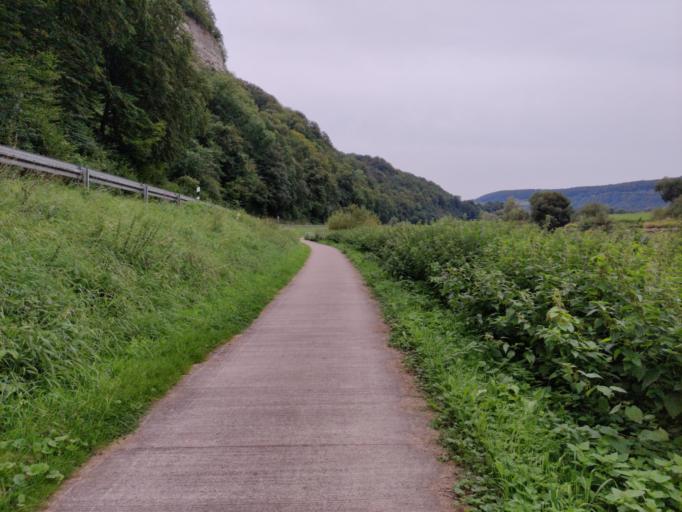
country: DE
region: Lower Saxony
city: Pegestorf
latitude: 51.9232
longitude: 9.4936
